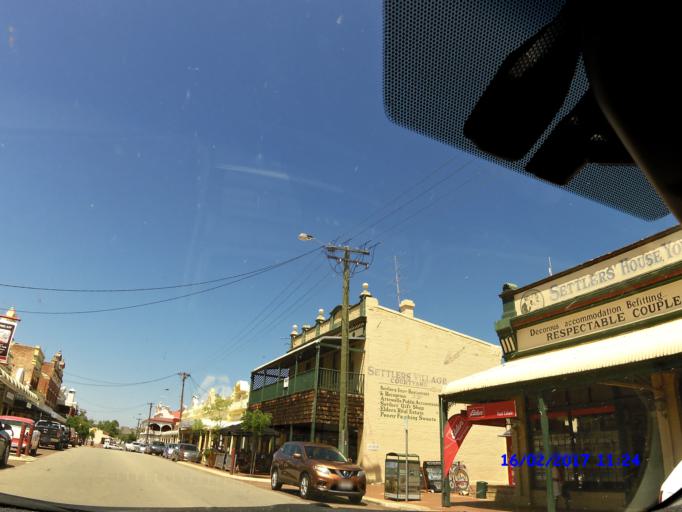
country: AU
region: Western Australia
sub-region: York
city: York
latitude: -31.8888
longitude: 116.7685
